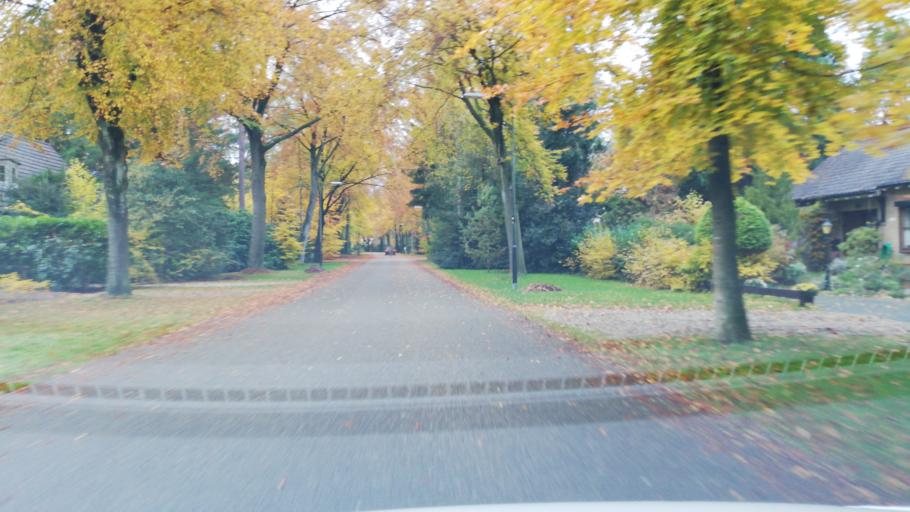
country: NL
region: Gelderland
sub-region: Gemeente Apeldoorn
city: Apeldoorn
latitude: 52.2221
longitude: 5.9299
